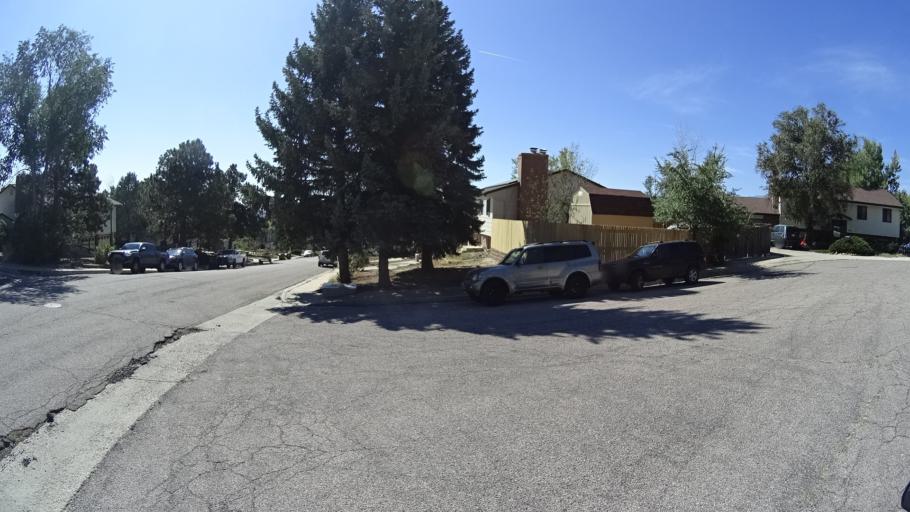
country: US
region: Colorado
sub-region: El Paso County
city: Cimarron Hills
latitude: 38.9119
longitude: -104.7652
